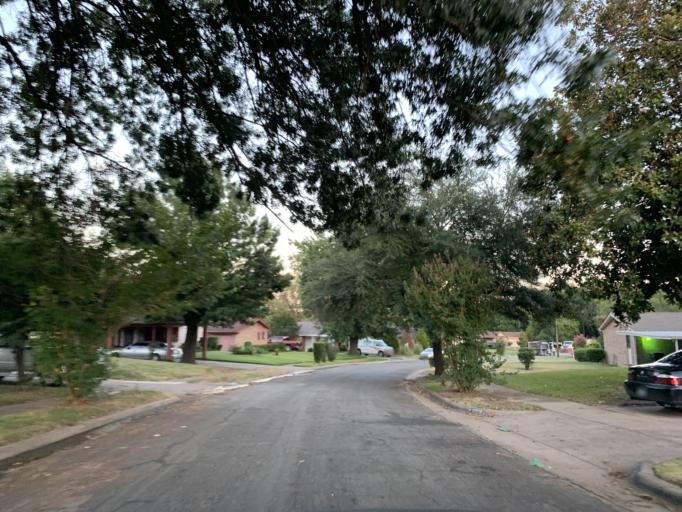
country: US
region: Texas
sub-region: Dallas County
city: Hutchins
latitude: 32.6719
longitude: -96.7980
